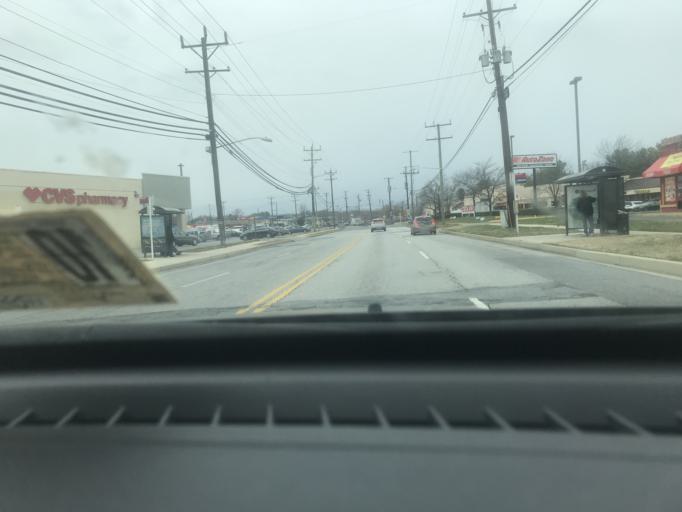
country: US
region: Maryland
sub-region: Prince George's County
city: Camp Springs
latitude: 38.7934
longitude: -76.9253
